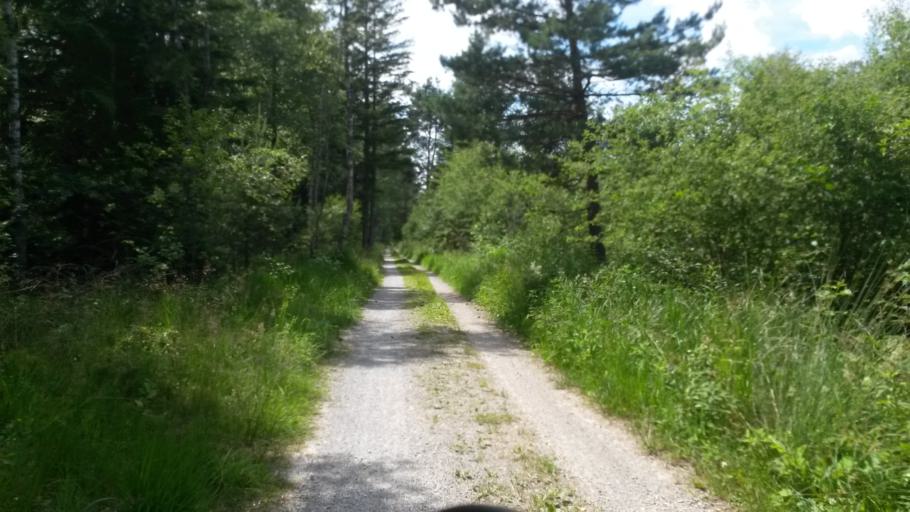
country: DE
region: Bavaria
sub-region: Upper Bavaria
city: Bernau am Chiemsee
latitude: 47.8136
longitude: 12.4088
